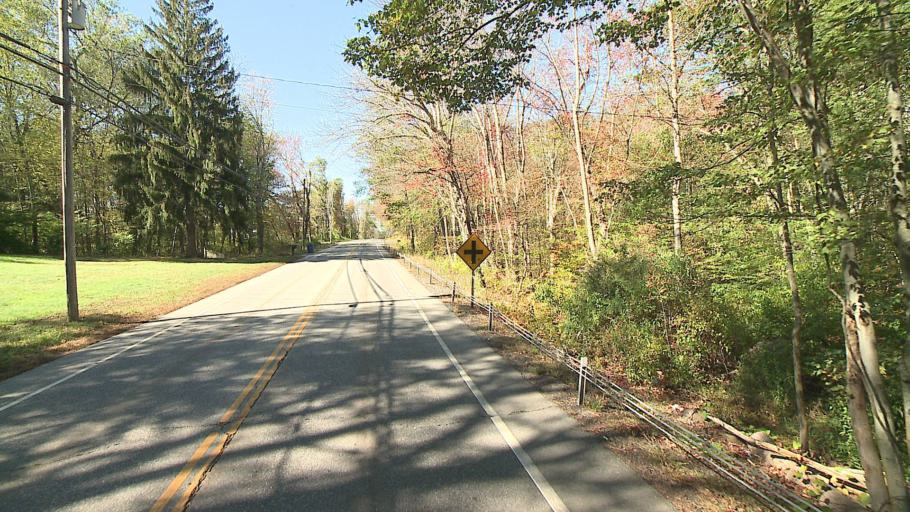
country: US
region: Connecticut
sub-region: Tolland County
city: Hebron
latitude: 41.6472
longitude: -72.4098
